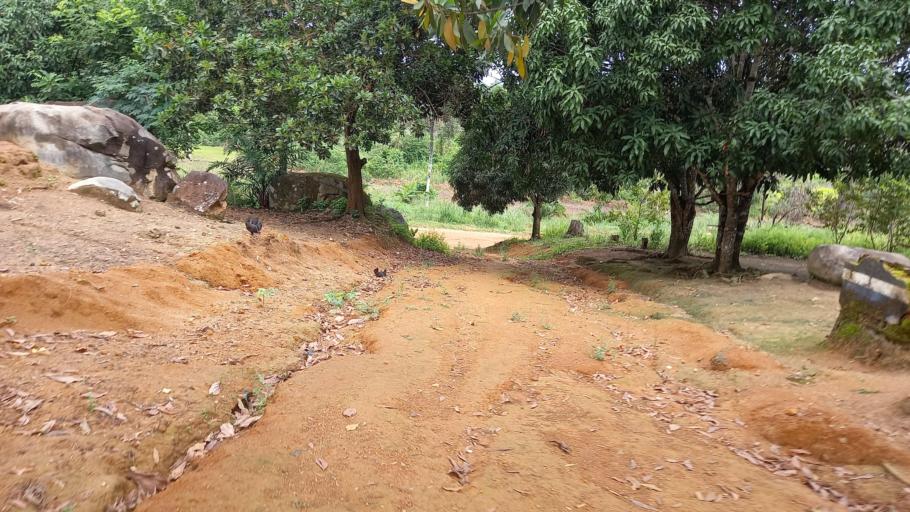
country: SL
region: Eastern Province
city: Kailahun
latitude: 8.2952
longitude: -10.5765
